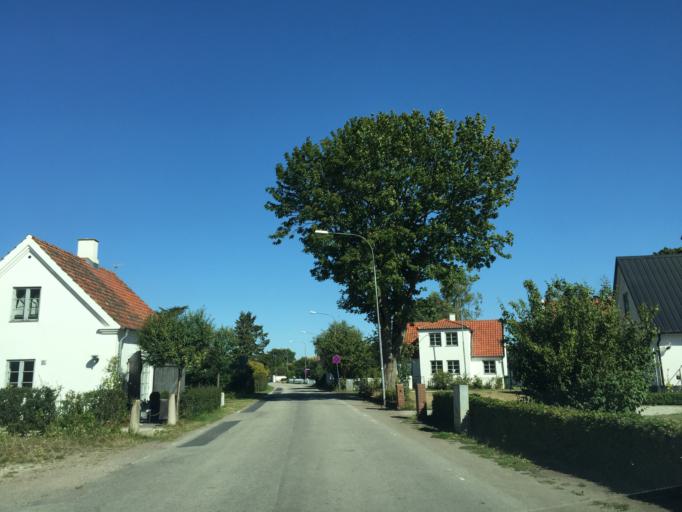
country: SE
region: Skane
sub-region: Ystads Kommun
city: Kopingebro
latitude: 55.3868
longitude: 14.0649
